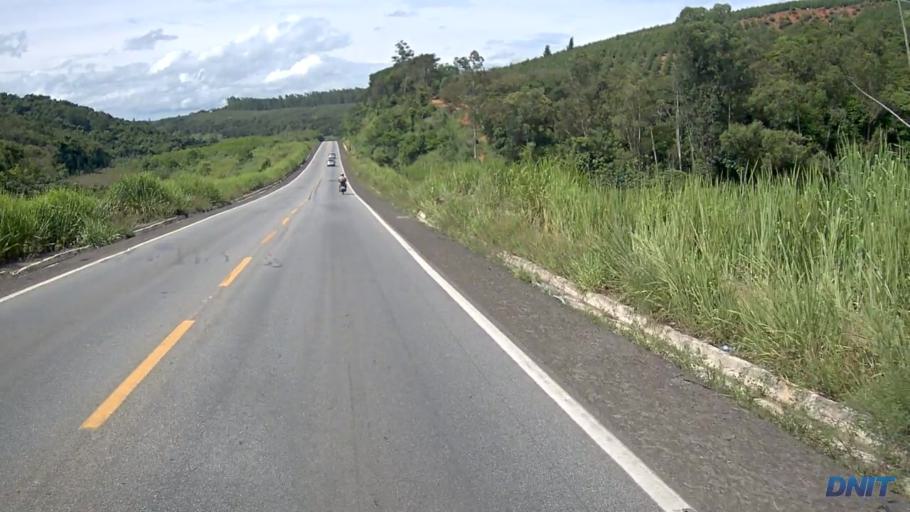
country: BR
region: Minas Gerais
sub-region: Ipaba
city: Ipaba
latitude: -19.4112
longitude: -42.4892
